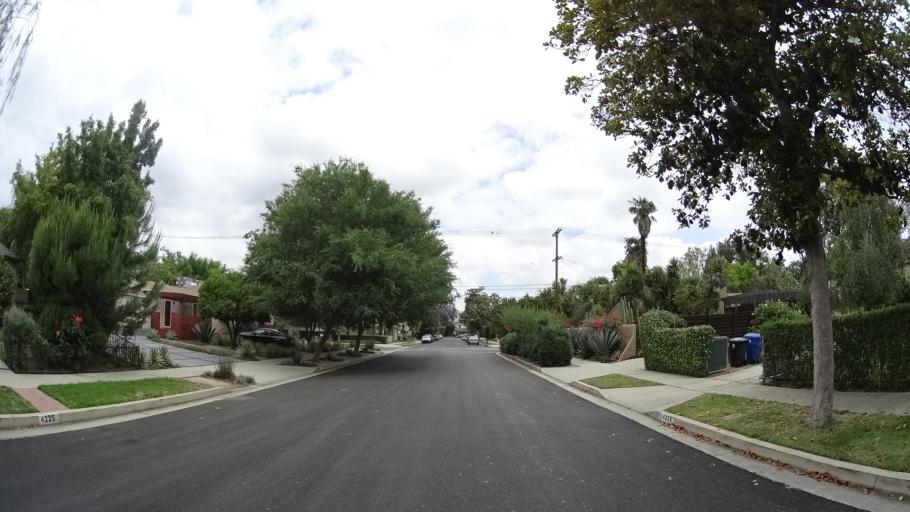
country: US
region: California
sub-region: Los Angeles County
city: Sherman Oaks
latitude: 34.1476
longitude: -118.4125
